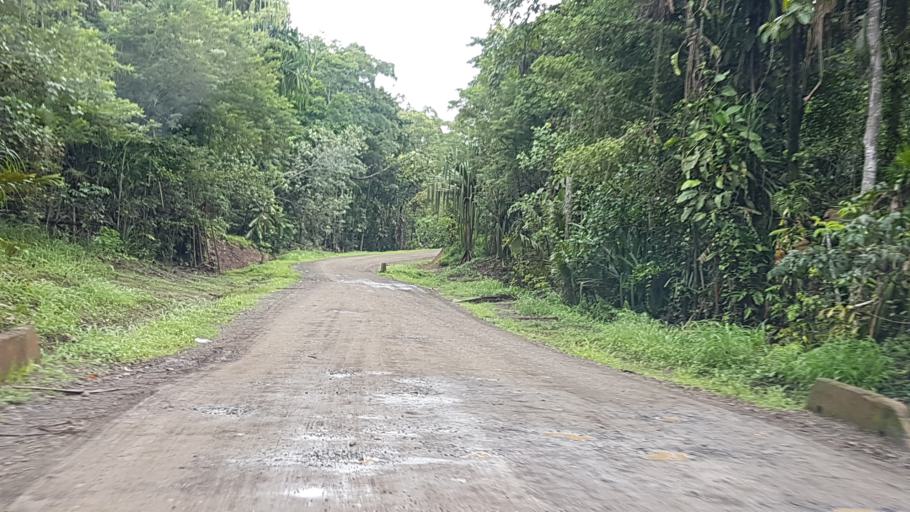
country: PG
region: Milne Bay
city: Alotau
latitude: -10.3389
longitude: 150.6108
